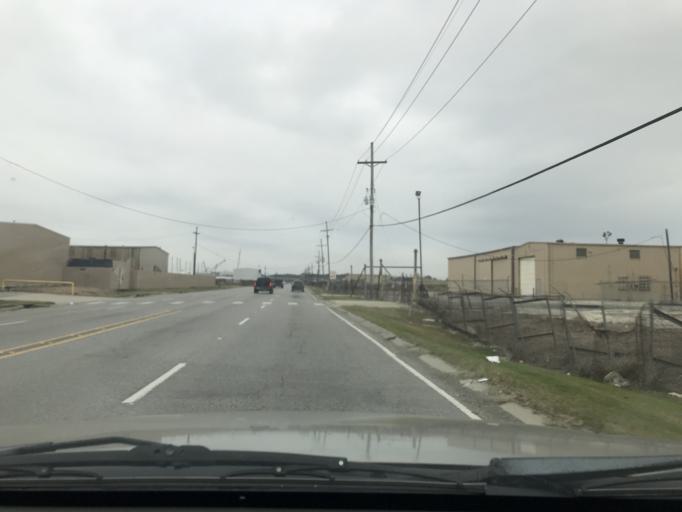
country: US
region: Louisiana
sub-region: Jefferson Parish
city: Harvey
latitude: 29.8811
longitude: -90.0758
